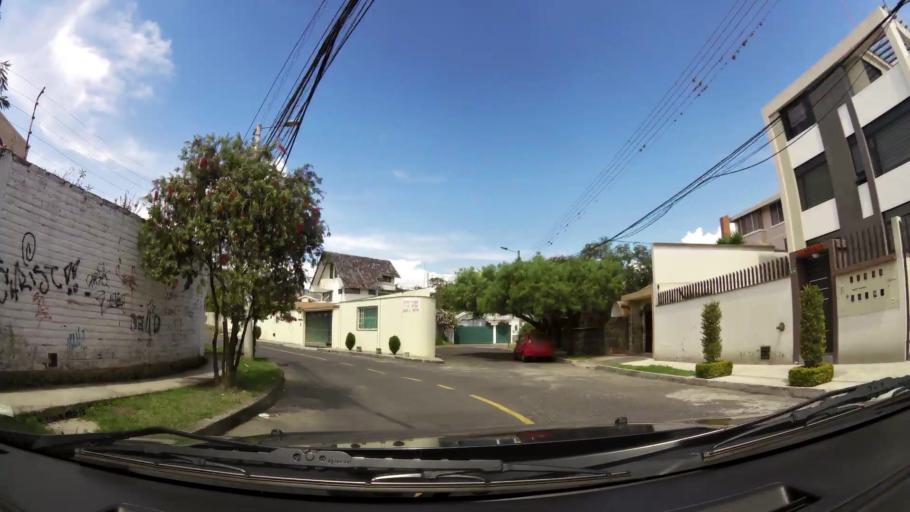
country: EC
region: Pichincha
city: Quito
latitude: -0.2135
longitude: -78.4296
